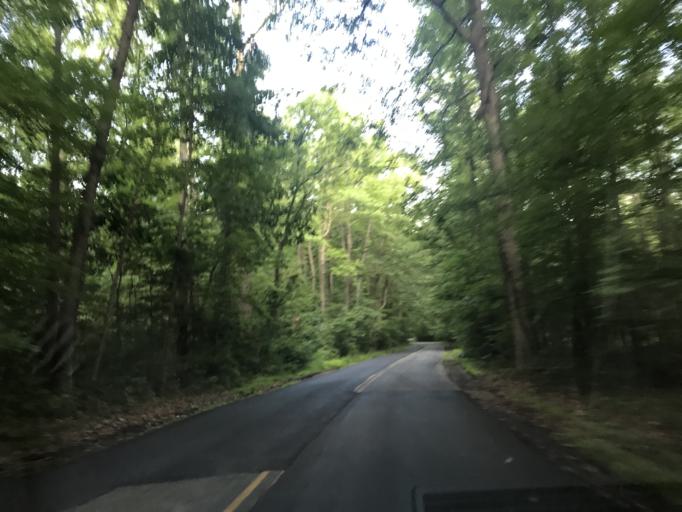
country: US
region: Maryland
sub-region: Harford County
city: Aberdeen
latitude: 39.5223
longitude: -76.2118
